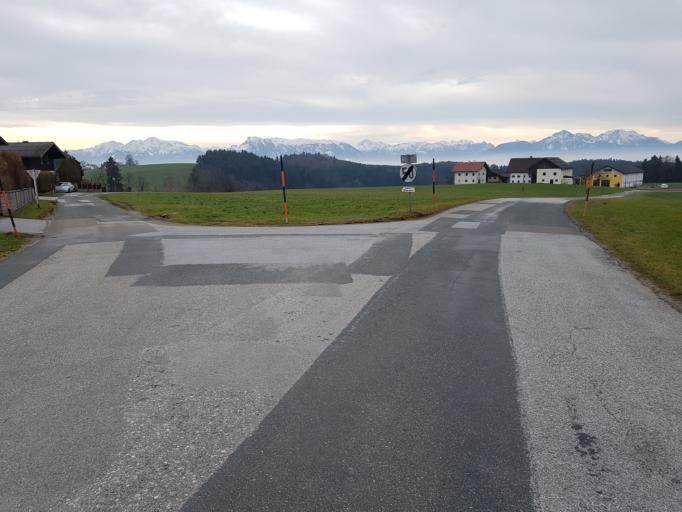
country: AT
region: Salzburg
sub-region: Politischer Bezirk Salzburg-Umgebung
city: Obertrum am See
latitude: 47.9218
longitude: 13.0436
